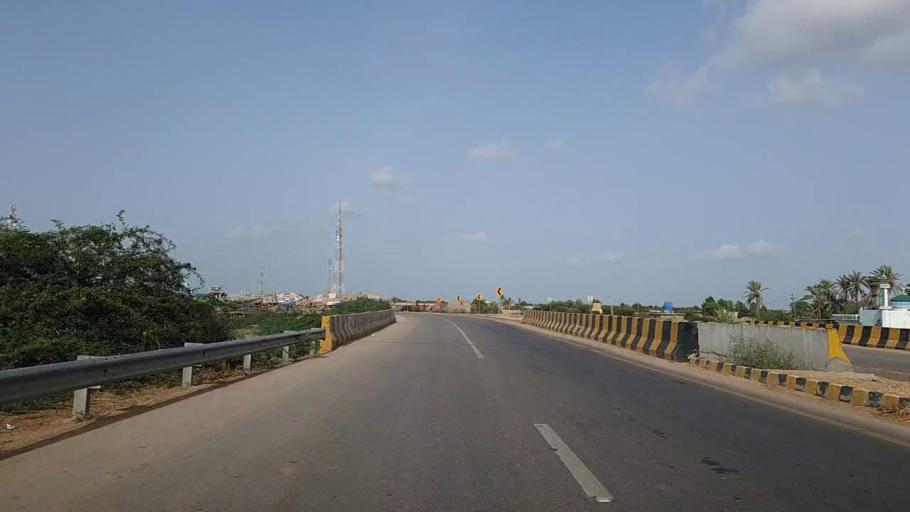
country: PK
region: Sindh
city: Thatta
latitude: 24.7401
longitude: 67.7641
